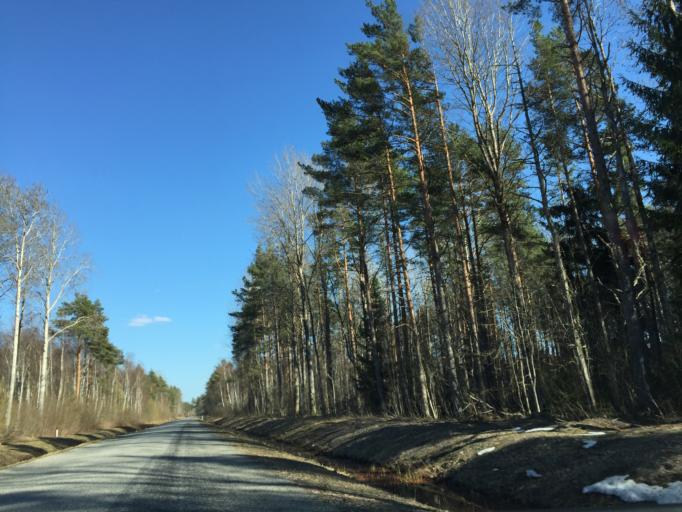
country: RU
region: Pskov
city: Gdov
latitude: 59.0102
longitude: 27.6354
